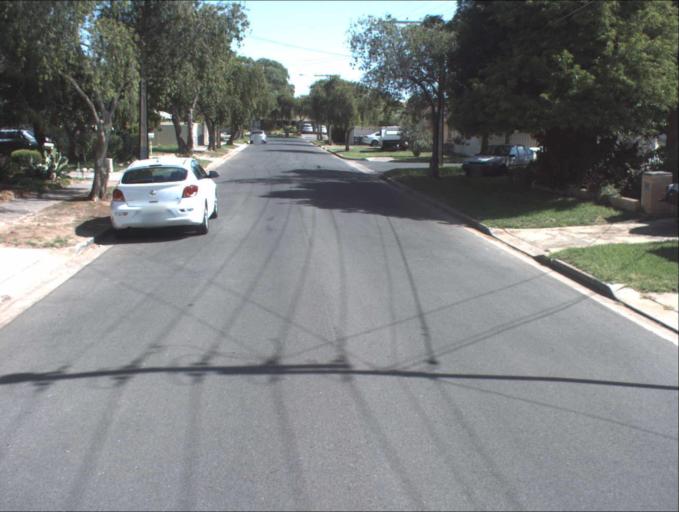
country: AU
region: South Australia
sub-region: Port Adelaide Enfield
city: Klemzig
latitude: -34.8798
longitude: 138.6423
